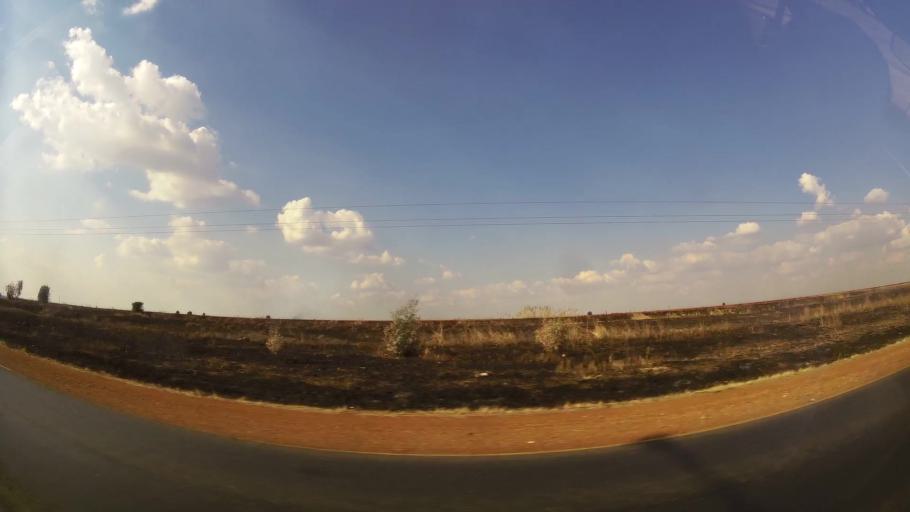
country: ZA
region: Gauteng
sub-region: Ekurhuleni Metropolitan Municipality
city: Brakpan
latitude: -26.3417
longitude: 28.3414
